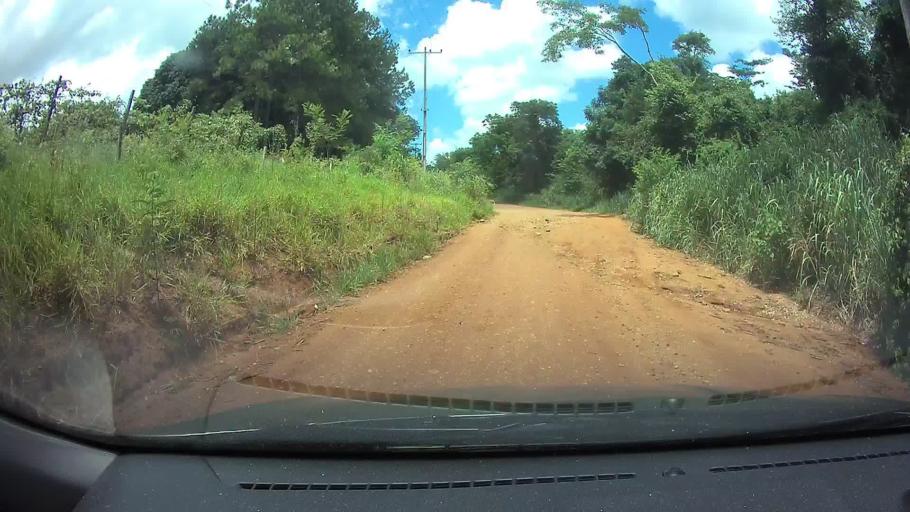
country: PY
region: Paraguari
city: La Colmena
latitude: -25.9245
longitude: -56.7931
